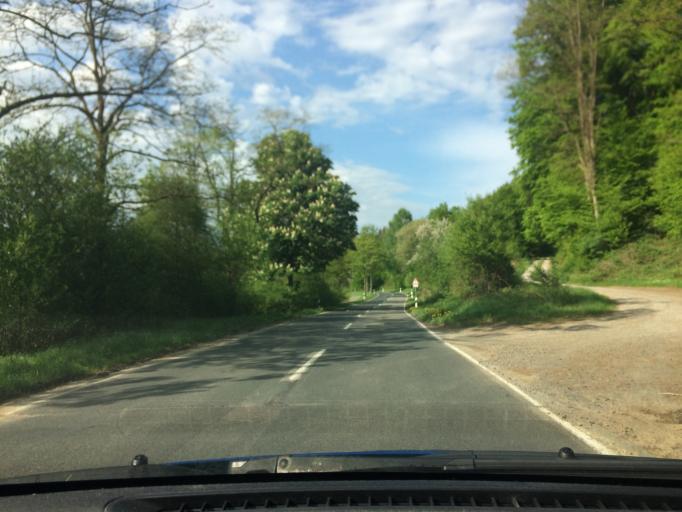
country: DE
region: Lower Saxony
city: Buhren
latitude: 51.5294
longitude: 9.6223
